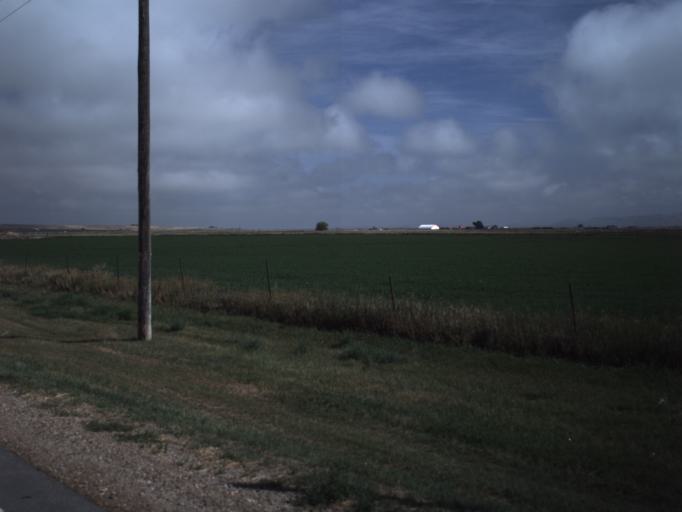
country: US
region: Utah
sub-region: Rich County
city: Randolph
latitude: 41.6706
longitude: -111.1850
